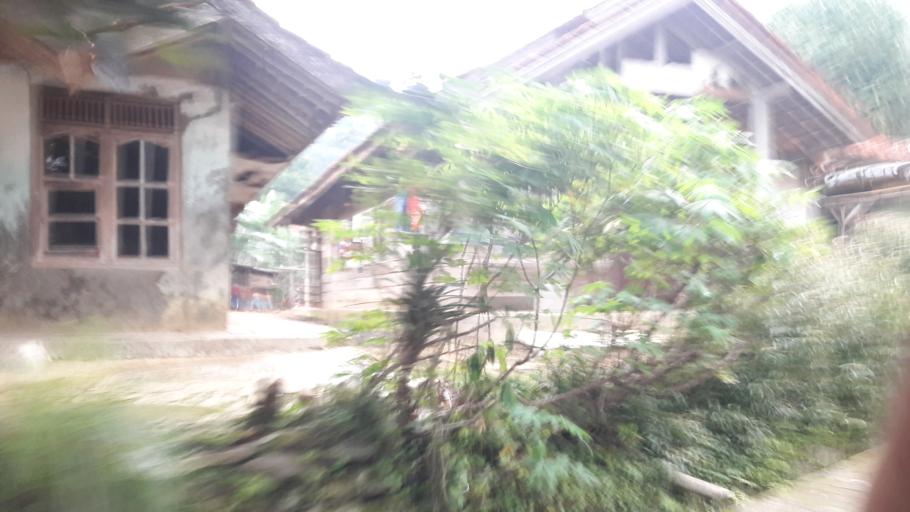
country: ID
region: West Java
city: Cipeundeuy
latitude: -6.6778
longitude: 106.5280
